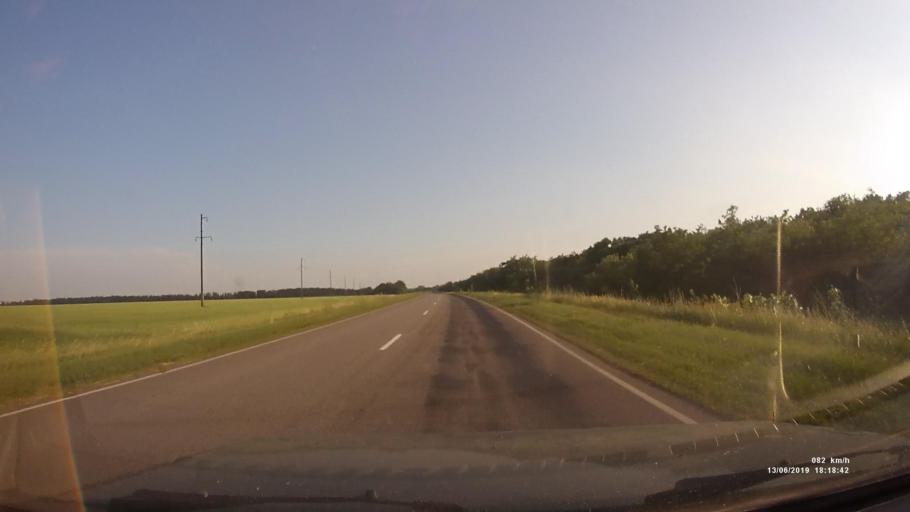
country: RU
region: Rostov
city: Kazanskaya
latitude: 49.9051
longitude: 41.3115
